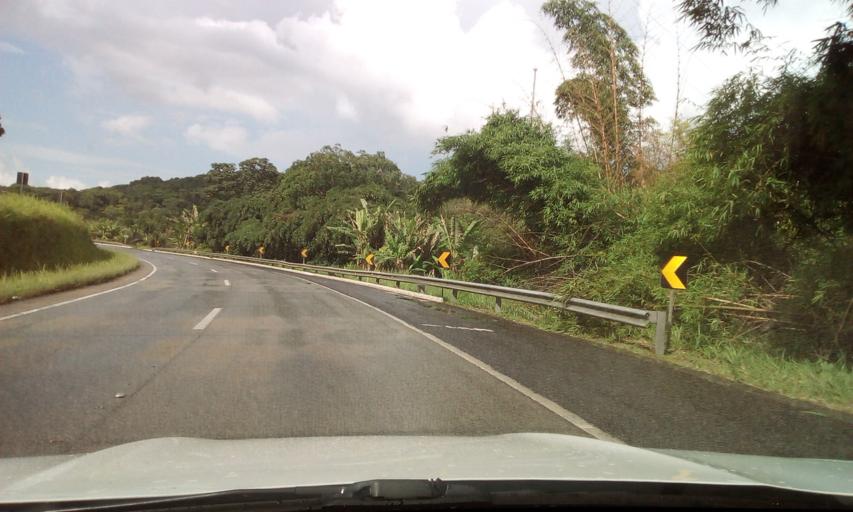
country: BR
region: Pernambuco
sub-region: Cabo De Santo Agostinho
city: Cabo
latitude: -8.3057
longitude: -35.0968
